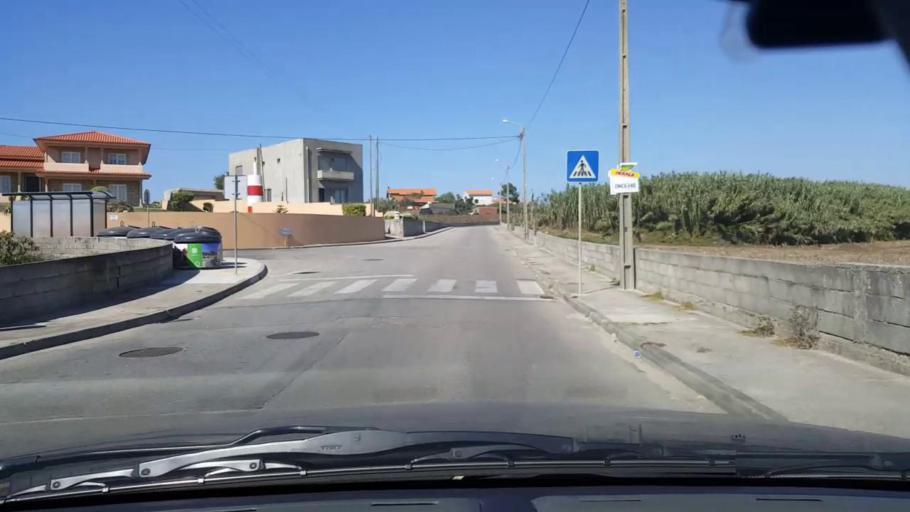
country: PT
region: Porto
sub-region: Matosinhos
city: Lavra
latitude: 41.2932
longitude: -8.7327
